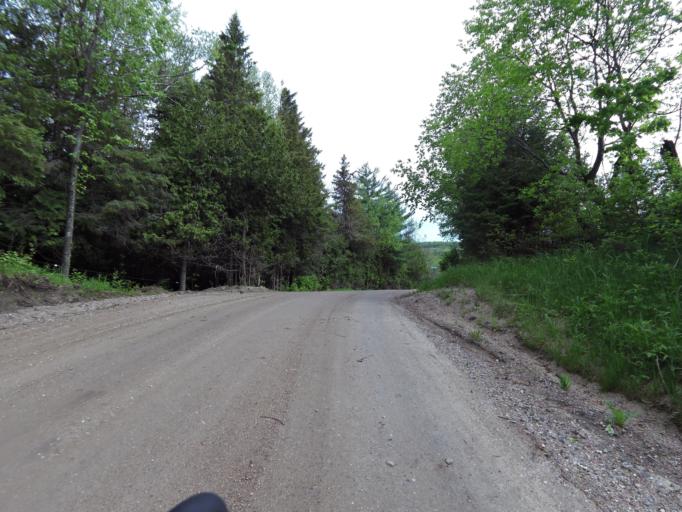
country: CA
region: Quebec
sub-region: Outaouais
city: Wakefield
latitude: 45.7325
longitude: -75.8903
